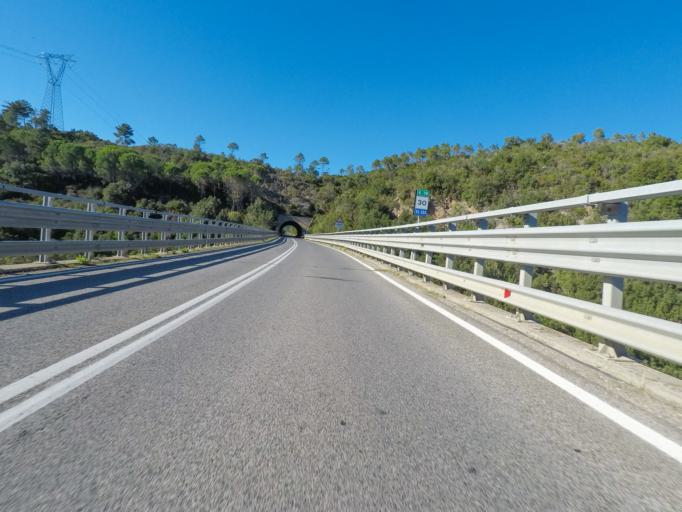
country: IT
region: Tuscany
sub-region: Provincia di Grosseto
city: Civitella Marittima
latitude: 43.0151
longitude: 11.2876
